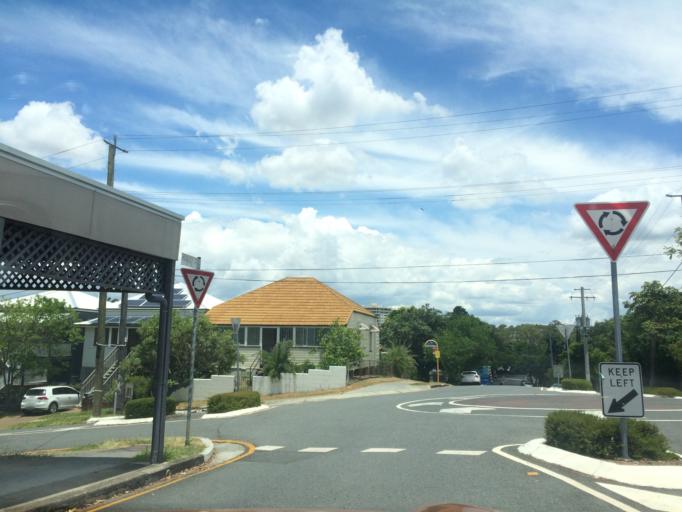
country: AU
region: Queensland
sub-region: Brisbane
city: Toowong
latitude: -27.4878
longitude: 153.0039
